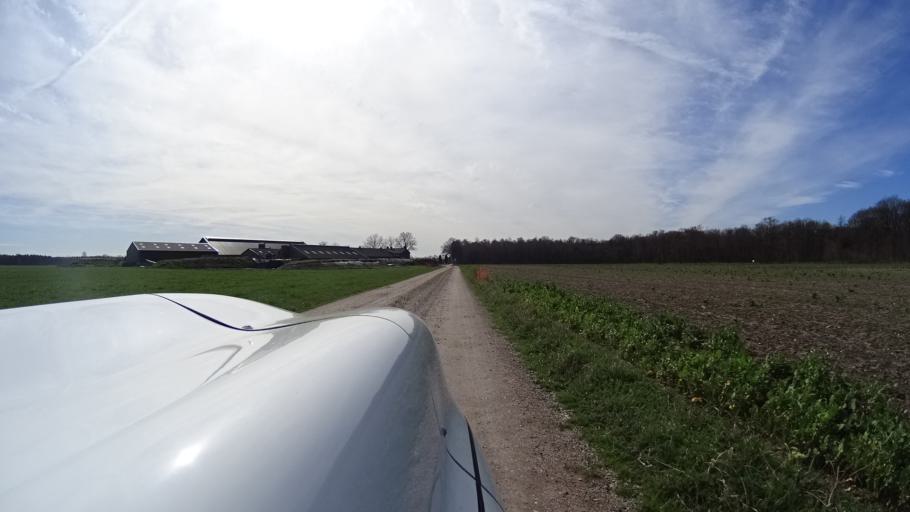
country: NL
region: Limburg
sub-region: Gemeente Venlo
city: Arcen
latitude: 51.5226
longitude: 6.2018
